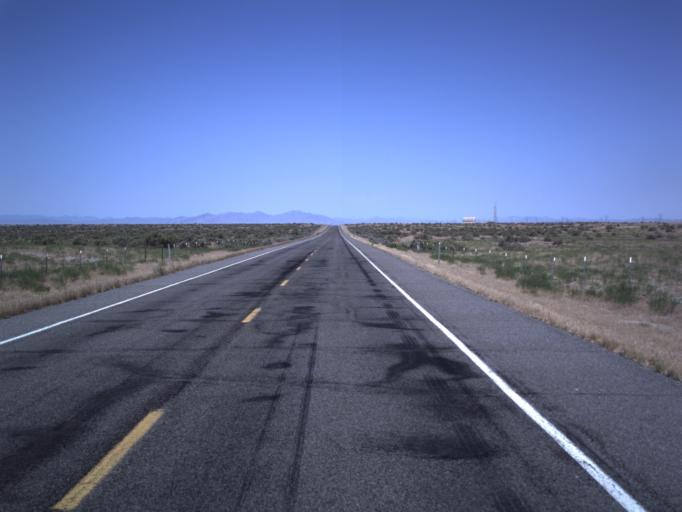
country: US
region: Utah
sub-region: Millard County
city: Delta
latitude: 39.4734
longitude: -112.4756
